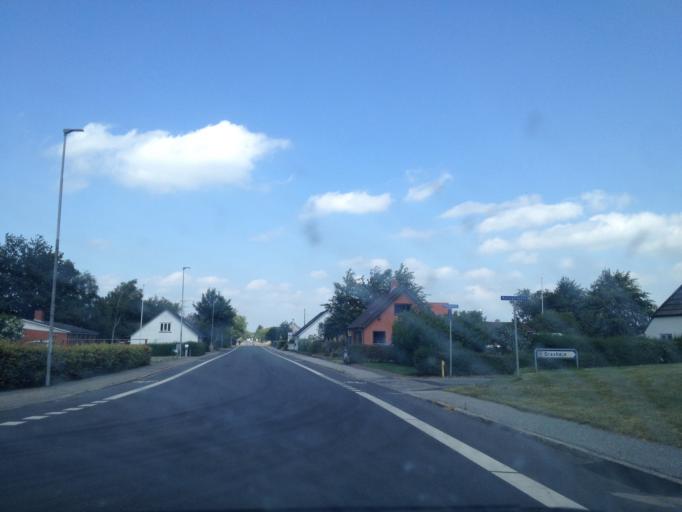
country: DK
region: South Denmark
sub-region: Kolding Kommune
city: Vamdrup
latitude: 55.4184
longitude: 9.2713
